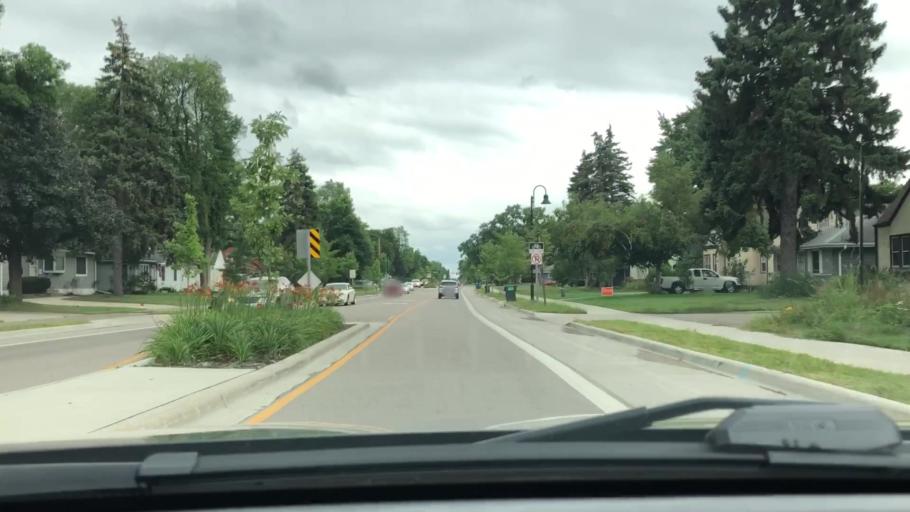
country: US
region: Minnesota
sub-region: Hennepin County
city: Richfield
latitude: 44.8798
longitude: -93.2680
